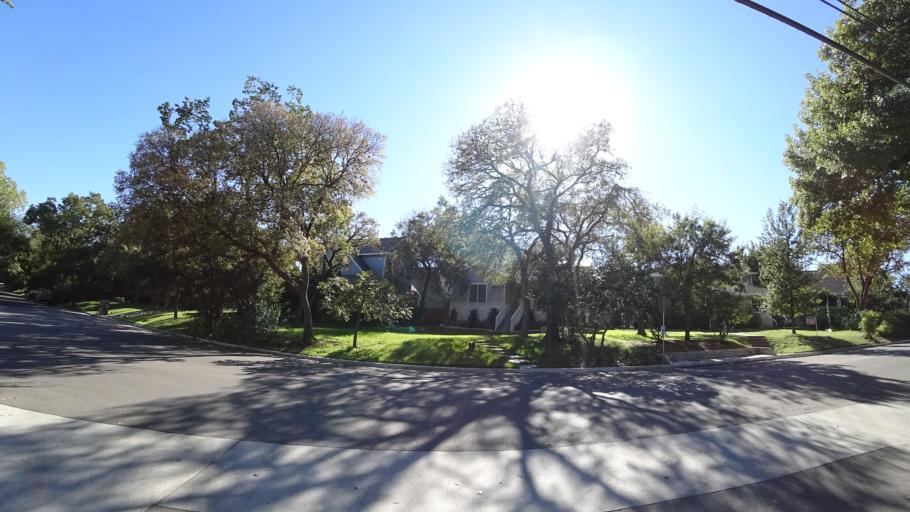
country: US
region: Texas
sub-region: Travis County
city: Austin
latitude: 30.3116
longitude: -97.7514
